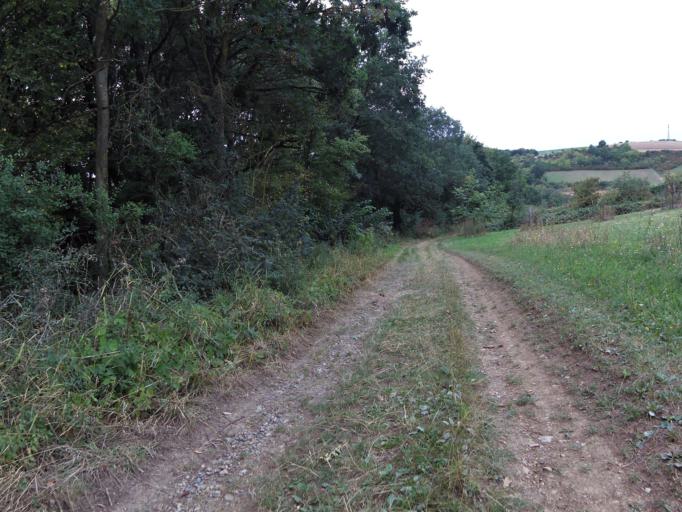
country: DE
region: Bavaria
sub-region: Regierungsbezirk Unterfranken
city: Rimpar
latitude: 49.8394
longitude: 9.9649
